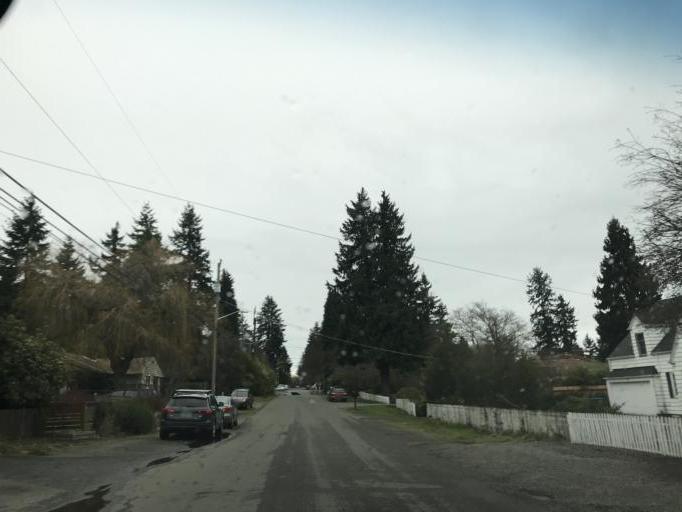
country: US
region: Washington
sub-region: King County
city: Lake Forest Park
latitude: 47.7077
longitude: -122.3044
